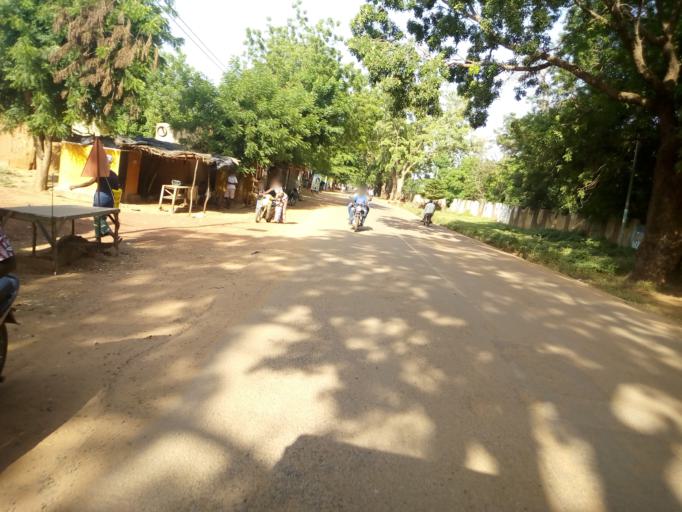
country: ML
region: Segou
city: Segou
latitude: 13.4419
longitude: -6.2739
